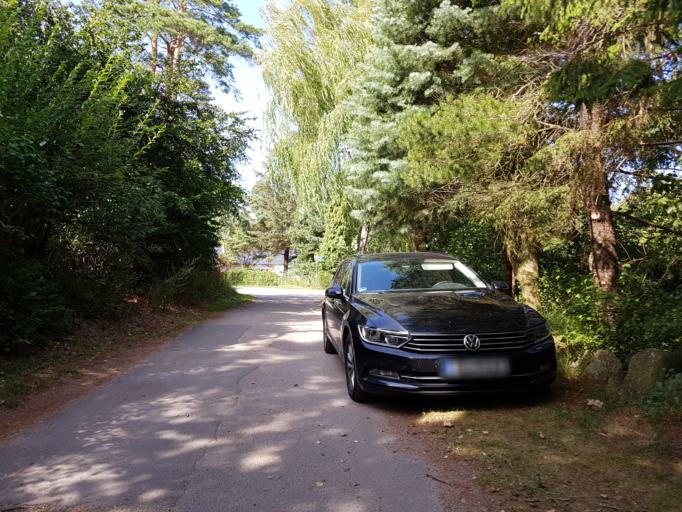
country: DK
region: Zealand
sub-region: Guldborgsund Kommune
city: Nykobing Falster
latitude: 54.6023
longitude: 11.9658
